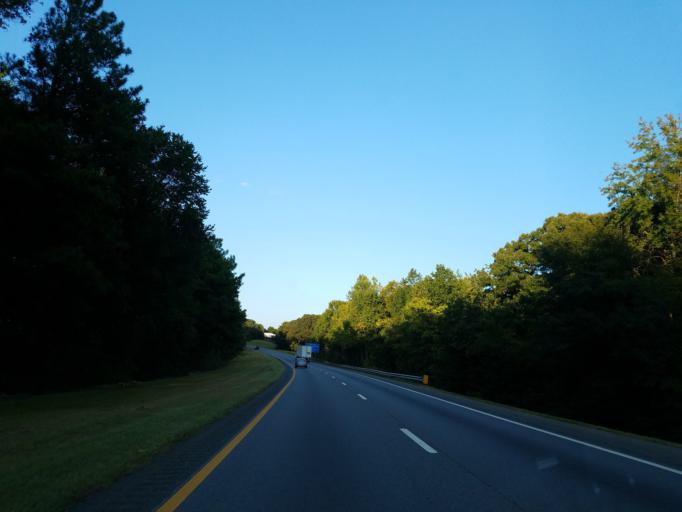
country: US
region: North Carolina
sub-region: Cleveland County
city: White Plains
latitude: 35.1723
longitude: -81.4234
